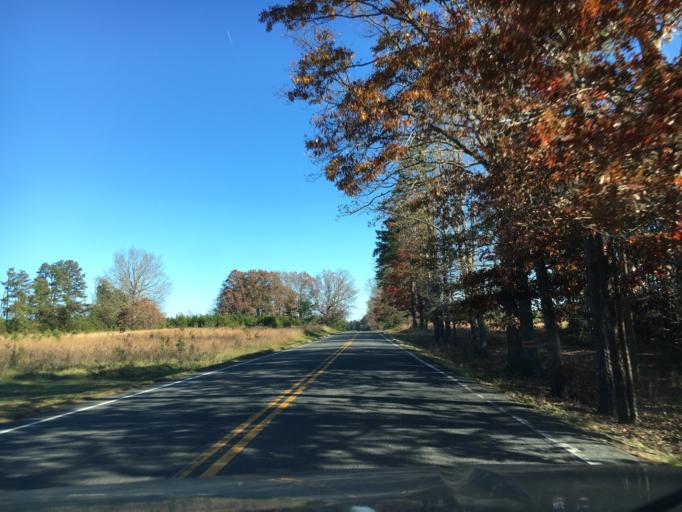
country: US
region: Virginia
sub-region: Buckingham County
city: Buckingham
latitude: 37.4870
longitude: -78.6418
